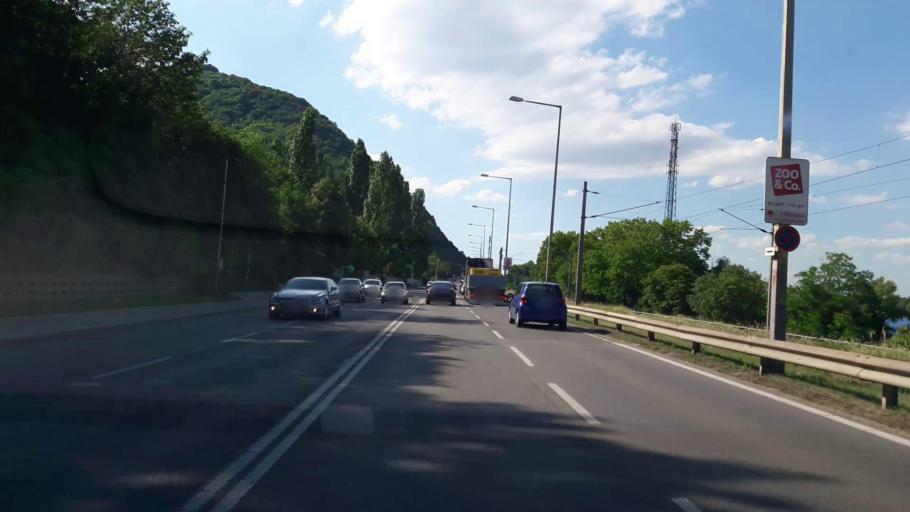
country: AT
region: Lower Austria
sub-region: Politischer Bezirk Korneuburg
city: Langenzersdorf
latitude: 48.2724
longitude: 16.3590
